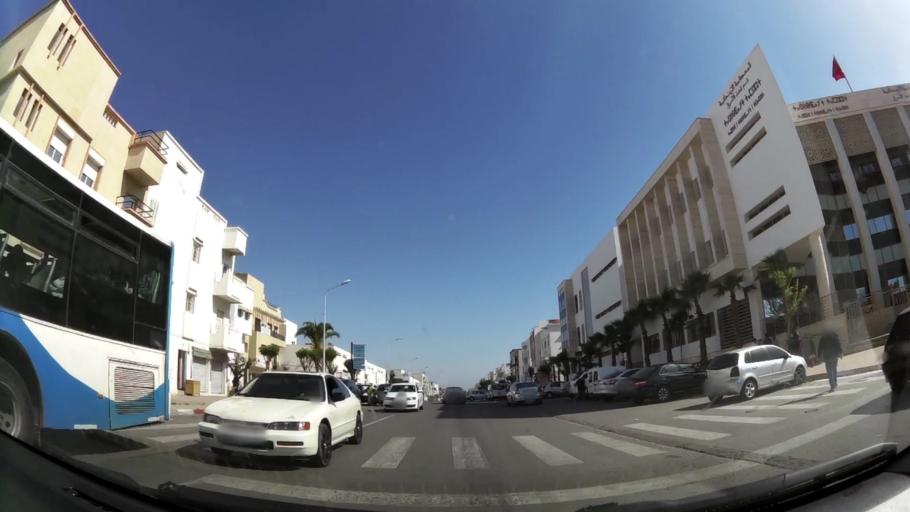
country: MA
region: Souss-Massa-Draa
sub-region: Agadir-Ida-ou-Tnan
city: Agadir
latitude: 30.4176
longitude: -9.5903
